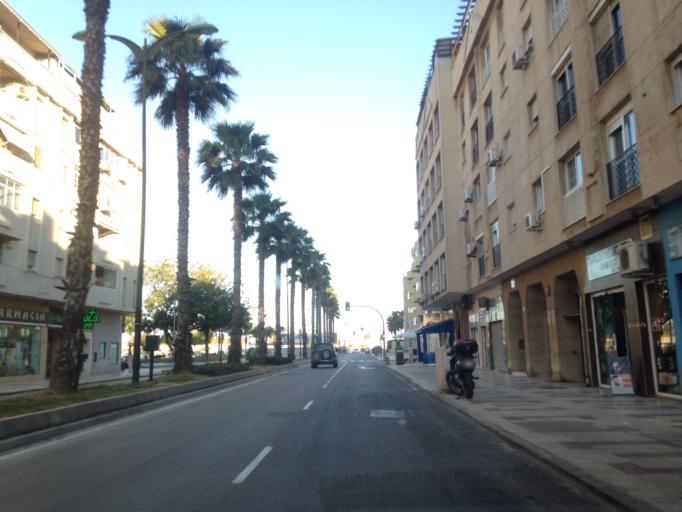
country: ES
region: Andalusia
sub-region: Provincia de Malaga
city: Malaga
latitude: 36.6856
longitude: -4.4506
